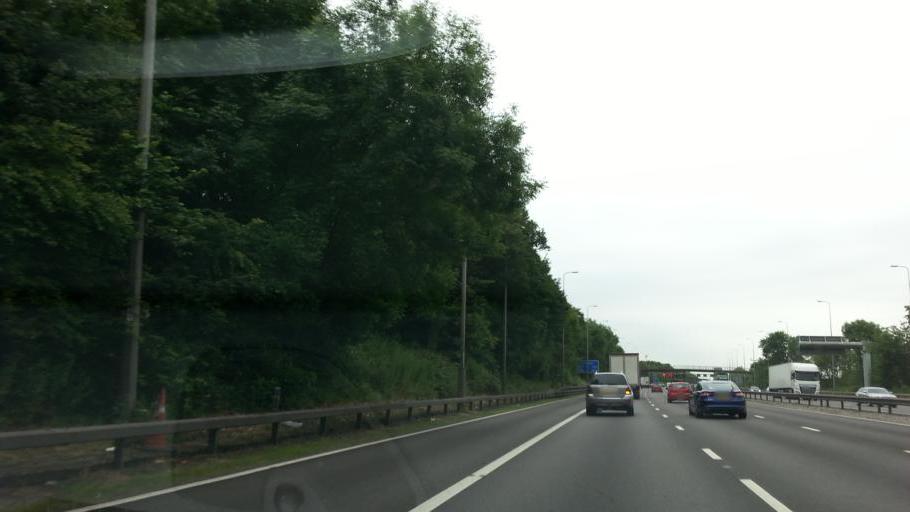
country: GB
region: England
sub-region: Solihull
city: Solihull
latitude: 52.3971
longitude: -1.7636
